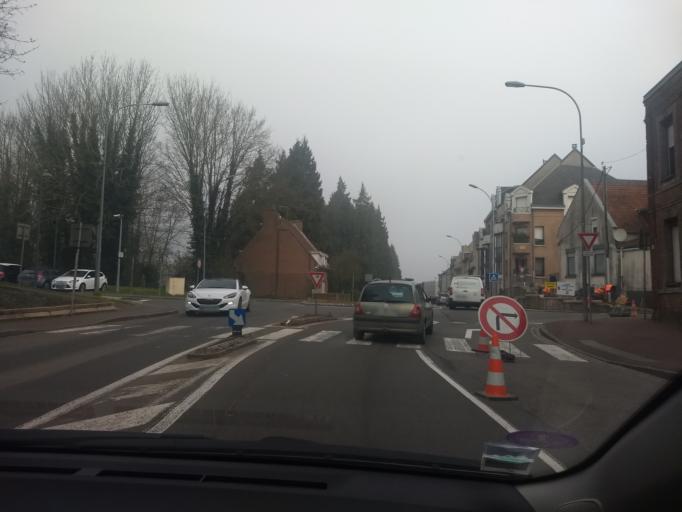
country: FR
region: Nord-Pas-de-Calais
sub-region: Departement du Pas-de-Calais
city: Saint-Omer
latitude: 50.7482
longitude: 2.2502
